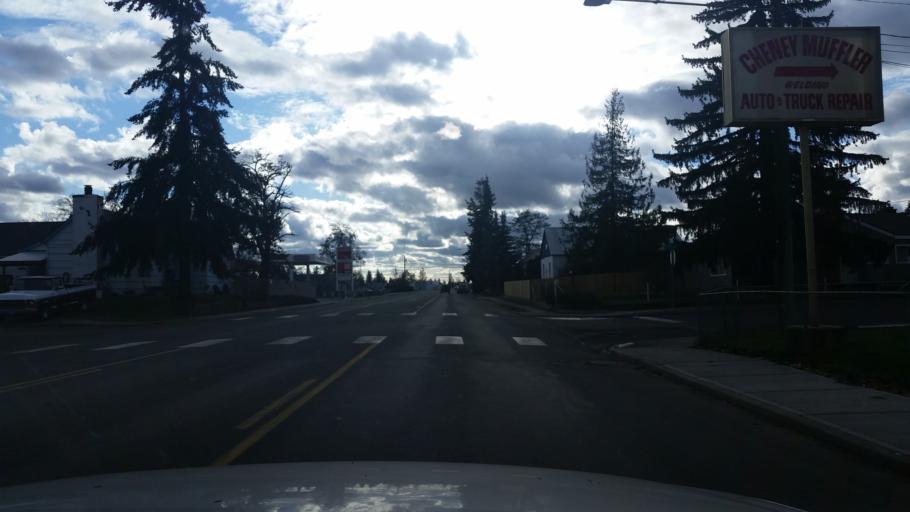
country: US
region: Washington
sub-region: Spokane County
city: Cheney
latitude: 47.4858
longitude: -117.5774
